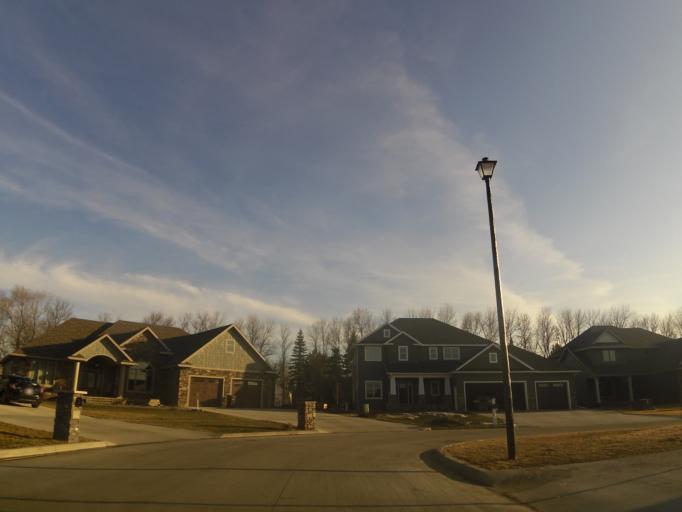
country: US
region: North Dakota
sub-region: Grand Forks County
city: Grand Forks
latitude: 47.8670
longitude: -97.0330
